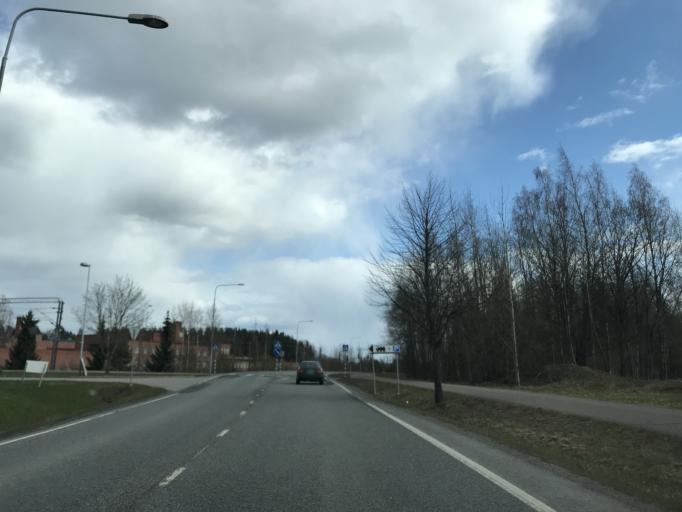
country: FI
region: Uusimaa
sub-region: Helsinki
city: Hyvinge
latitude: 60.5508
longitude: 24.9732
